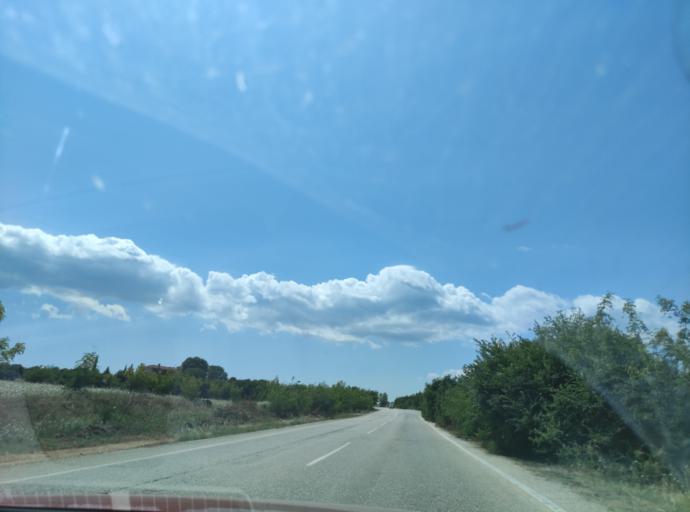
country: GR
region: East Macedonia and Thrace
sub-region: Nomos Dramas
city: Fotolivos
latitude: 40.9912
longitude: 24.0793
